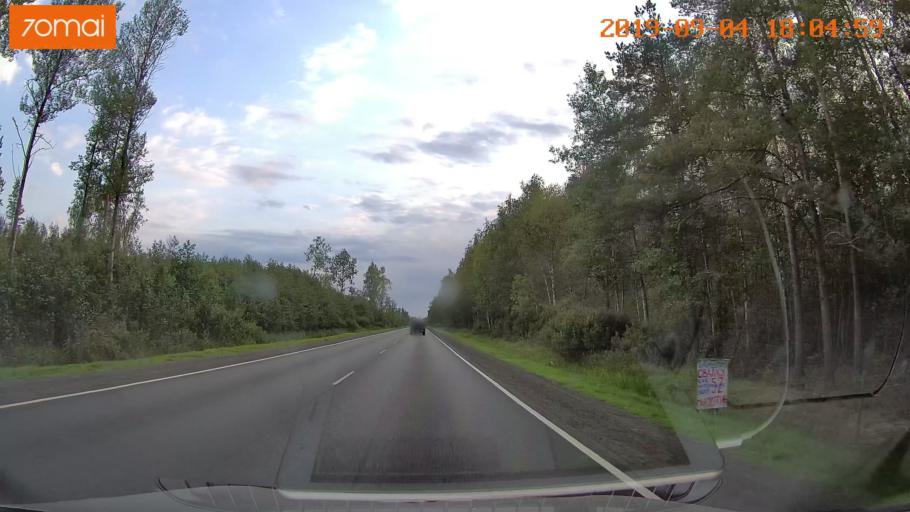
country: RU
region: Moskovskaya
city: Il'inskiy Pogost
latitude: 55.4462
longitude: 38.8321
